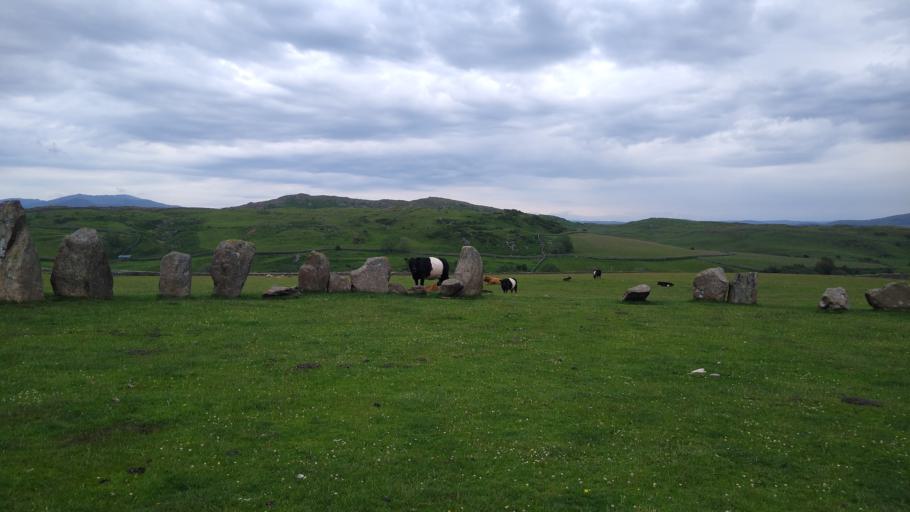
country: GB
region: England
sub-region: Cumbria
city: Millom
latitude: 54.2825
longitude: -3.2741
